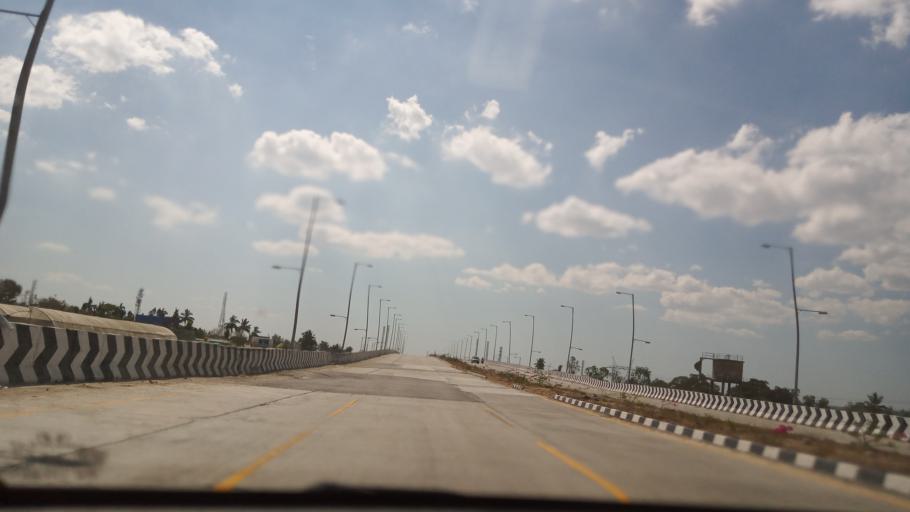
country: IN
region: Andhra Pradesh
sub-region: Chittoor
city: Palmaner
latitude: 13.2215
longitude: 78.7380
